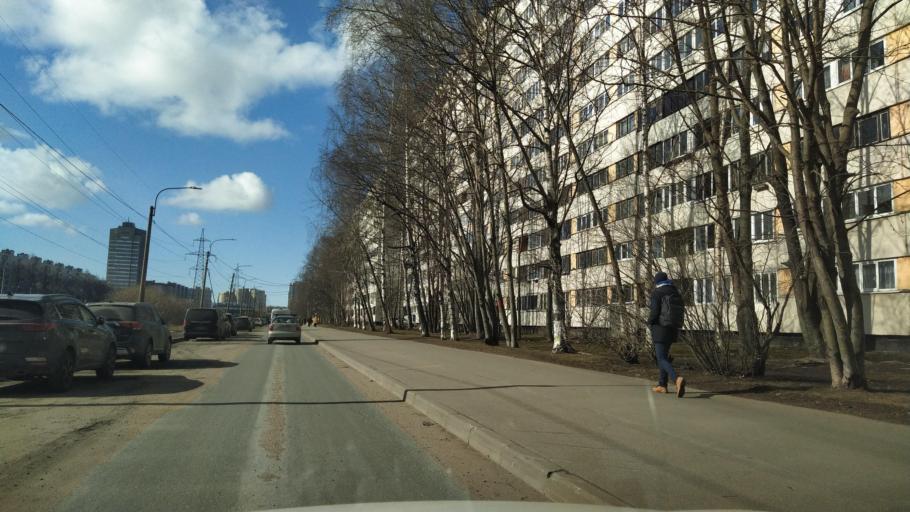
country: RU
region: St.-Petersburg
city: Komendantsky aerodrom
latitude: 60.0051
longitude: 30.2864
